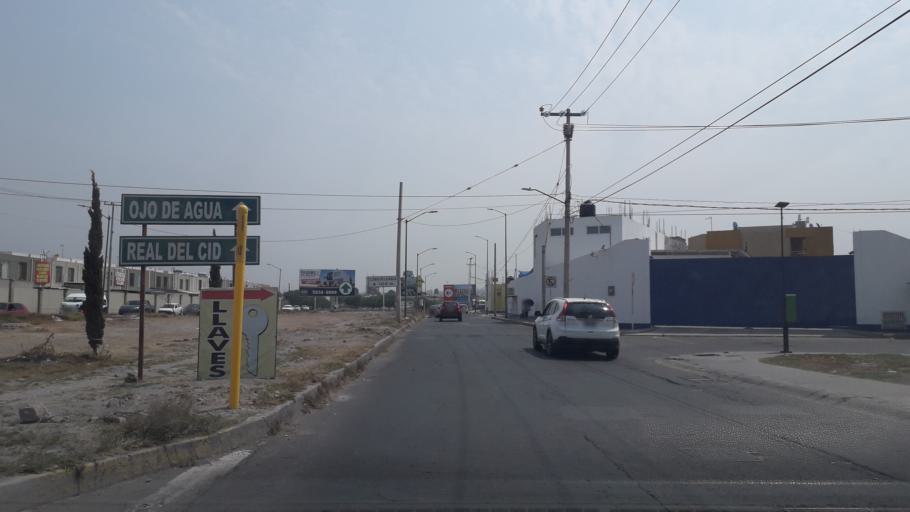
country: MX
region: Mexico
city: Santo Tomas Chiconautla
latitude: 19.6397
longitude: -99.0241
